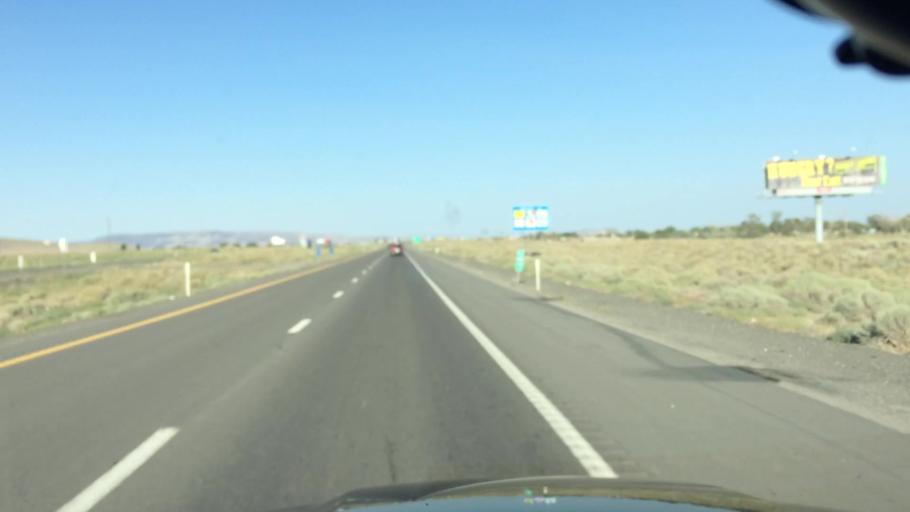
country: US
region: Nevada
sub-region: Lyon County
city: Fernley
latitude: 39.6150
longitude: -119.2508
